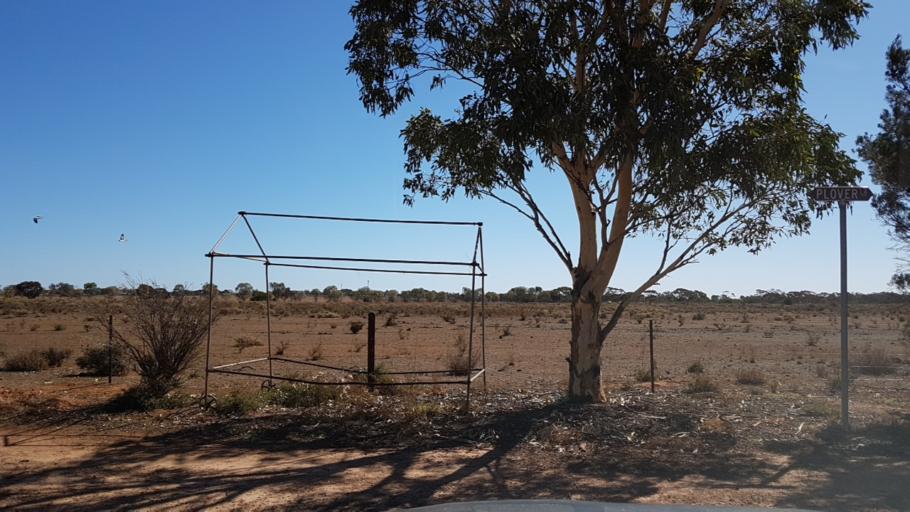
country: AU
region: South Australia
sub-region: Peterborough
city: Peterborough
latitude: -32.9828
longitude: 138.8496
